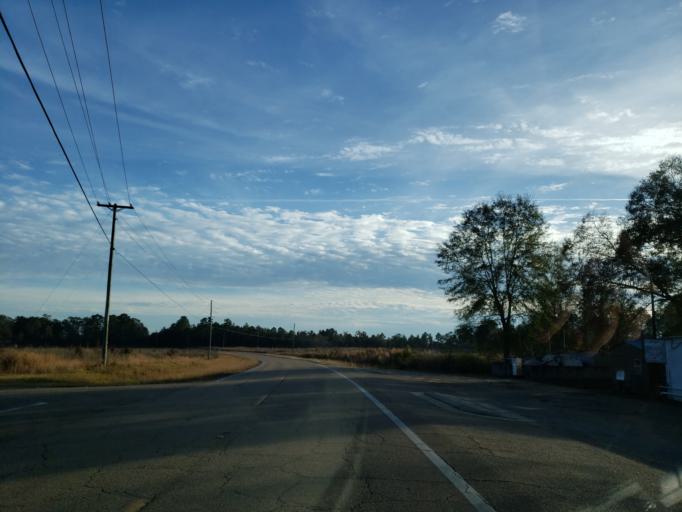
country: US
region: Mississippi
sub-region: Lamar County
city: West Hattiesburg
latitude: 31.2704
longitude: -89.4664
